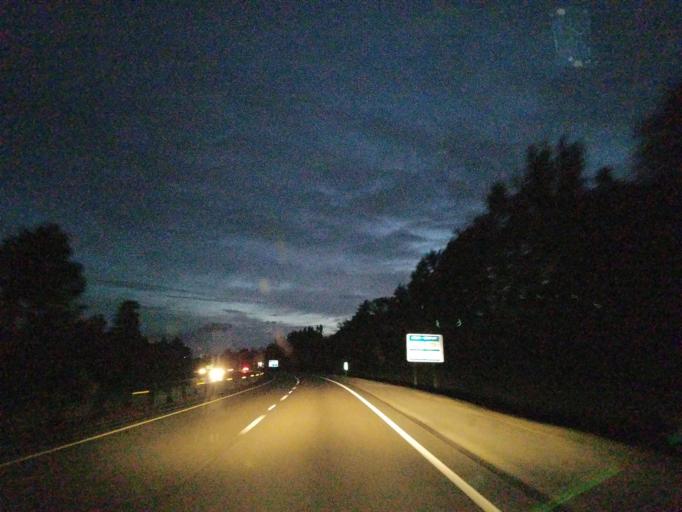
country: US
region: Mississippi
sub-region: Jones County
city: Laurel
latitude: 31.7067
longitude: -89.1156
